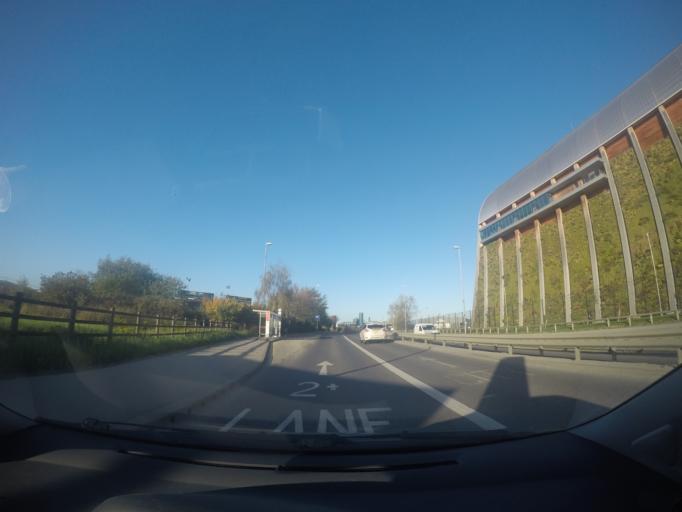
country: GB
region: England
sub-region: City and Borough of Leeds
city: Leeds
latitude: 53.7868
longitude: -1.5037
